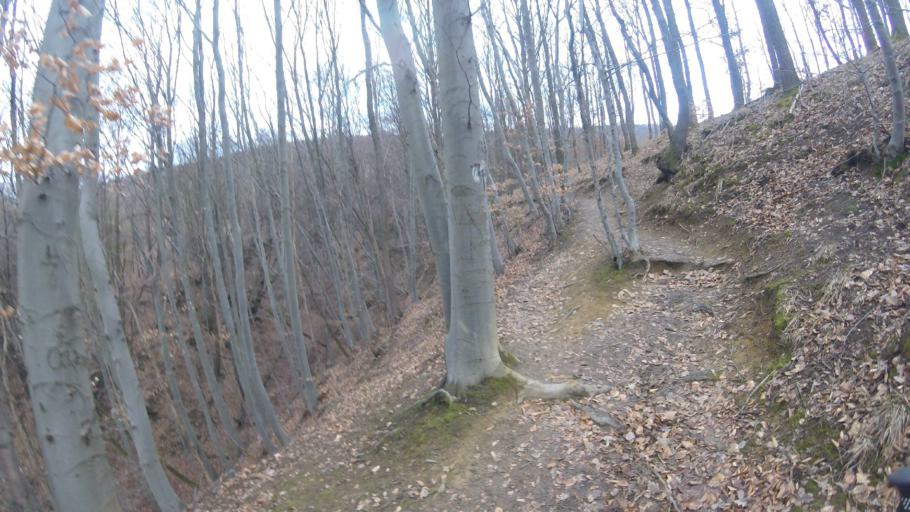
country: HU
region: Pest
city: Pilisszentkereszt
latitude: 47.6915
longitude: 18.9133
